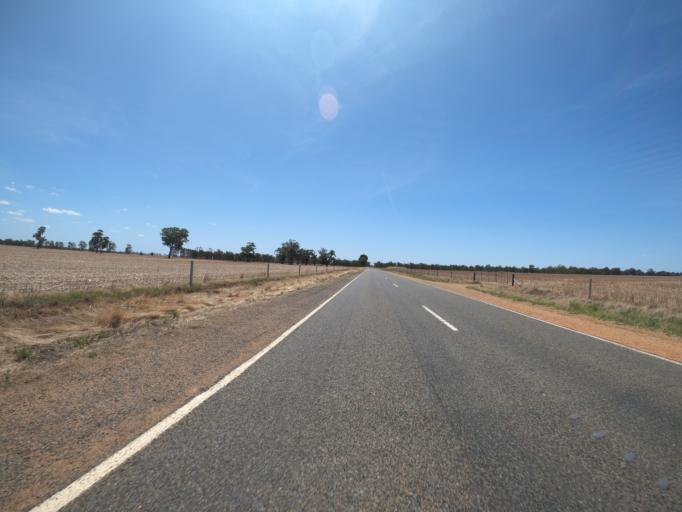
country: AU
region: Victoria
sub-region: Moira
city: Yarrawonga
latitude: -36.1670
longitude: 145.9672
